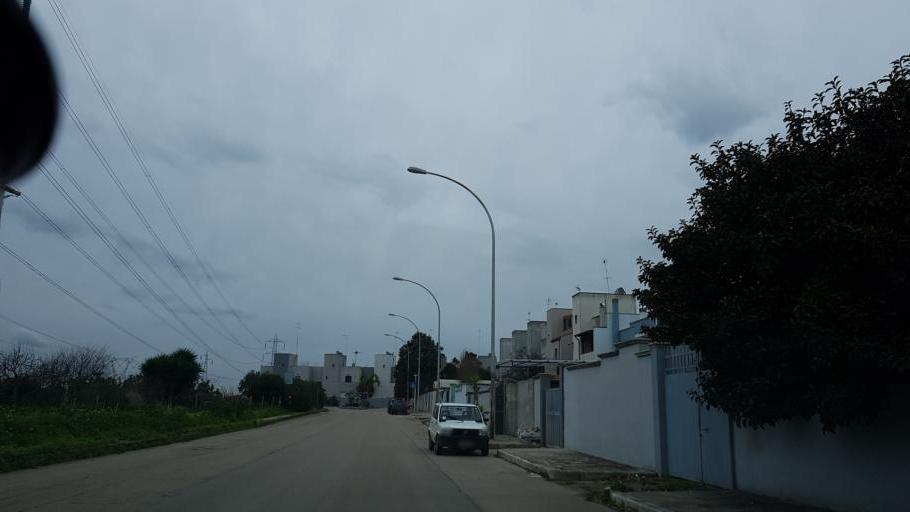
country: IT
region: Apulia
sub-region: Provincia di Brindisi
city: La Rosa
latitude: 40.6039
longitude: 17.9542
